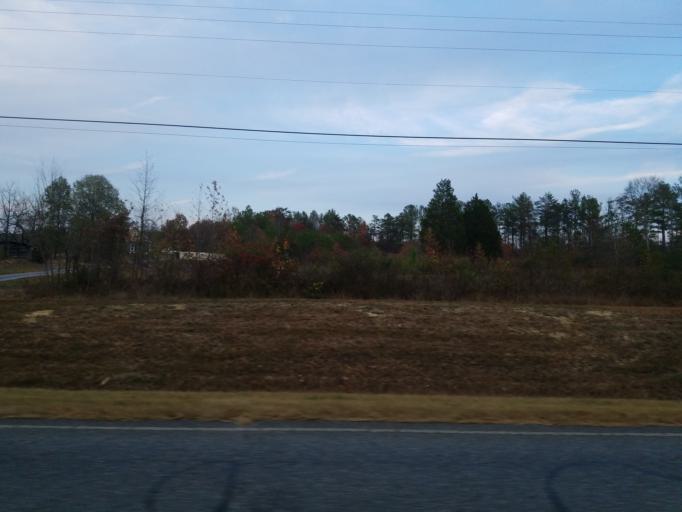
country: US
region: Georgia
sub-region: Murray County
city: Chatsworth
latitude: 34.5978
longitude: -84.7535
